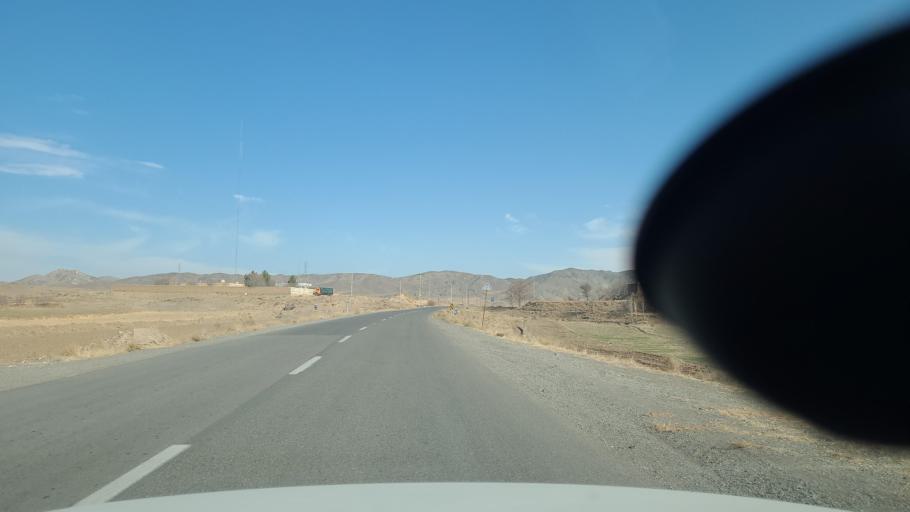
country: IR
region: Razavi Khorasan
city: Fariman
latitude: 35.5959
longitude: 59.6952
